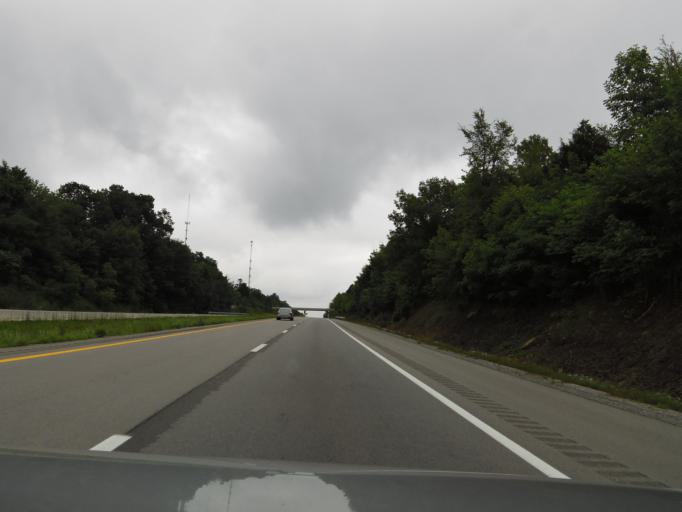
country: US
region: Kentucky
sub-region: Ohio County
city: Oak Grove
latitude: 37.4093
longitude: -86.5422
